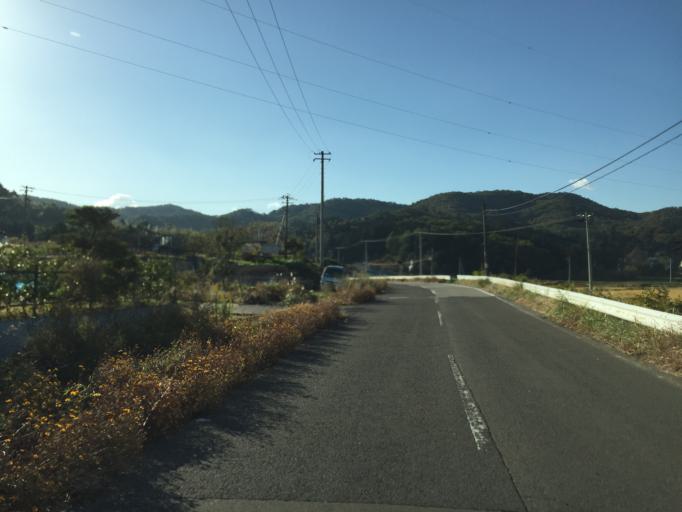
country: JP
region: Fukushima
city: Yanagawamachi-saiwaicho
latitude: 37.9256
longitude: 140.6116
